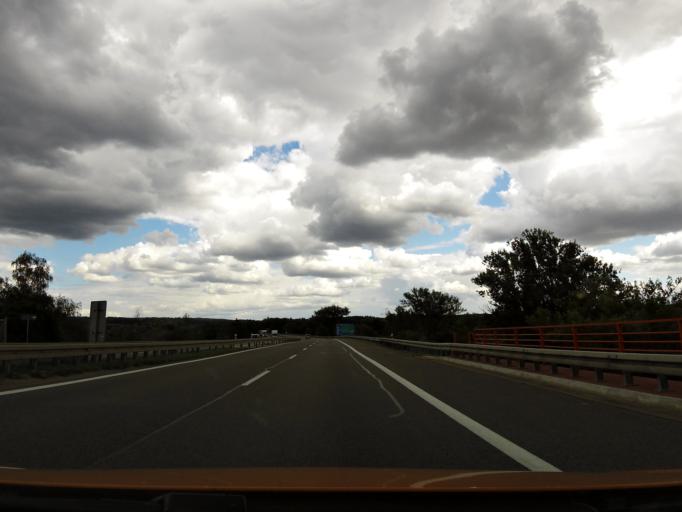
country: PL
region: West Pomeranian Voivodeship
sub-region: Powiat policki
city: Przeclaw
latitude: 53.3333
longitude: 14.5327
